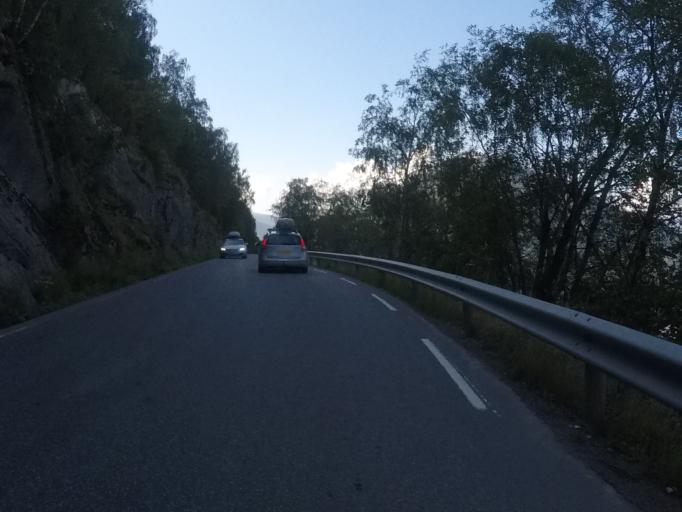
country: NO
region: Sogn og Fjordane
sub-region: Vik
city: Vikoyri
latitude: 61.1149
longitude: 6.6002
